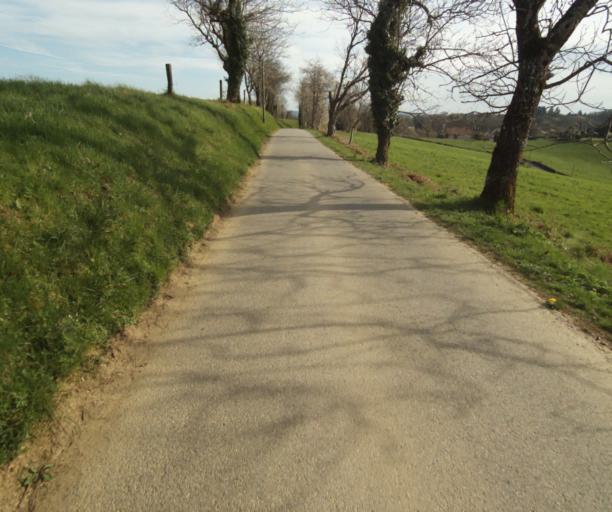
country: FR
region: Limousin
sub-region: Departement de la Correze
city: Naves
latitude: 45.3163
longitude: 1.7472
